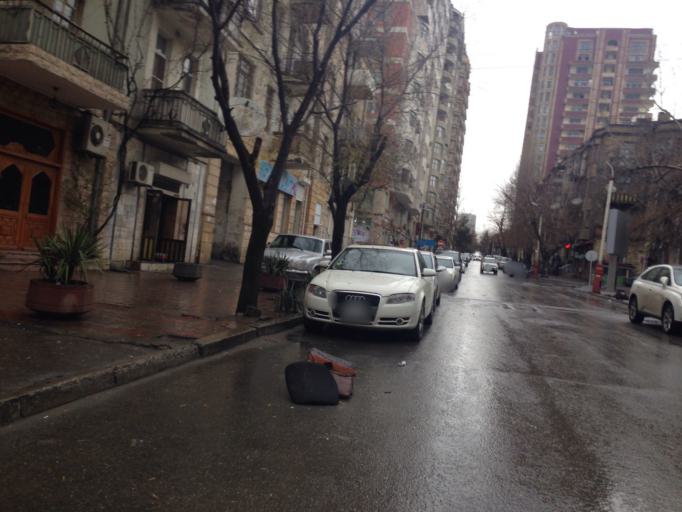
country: AZ
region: Baki
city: Baku
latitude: 40.3799
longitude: 49.8457
